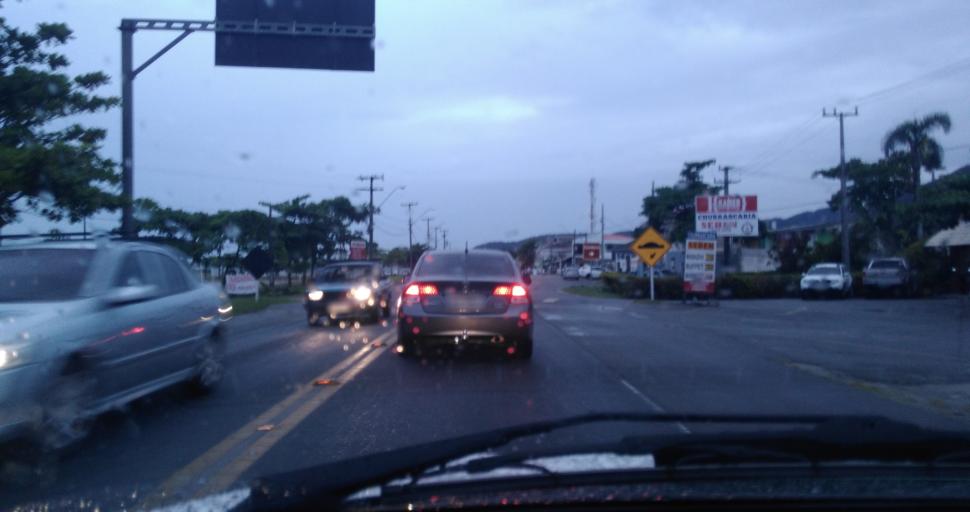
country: BR
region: Parana
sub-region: Guaratuba
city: Guaratuba
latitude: -25.8068
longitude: -48.5313
